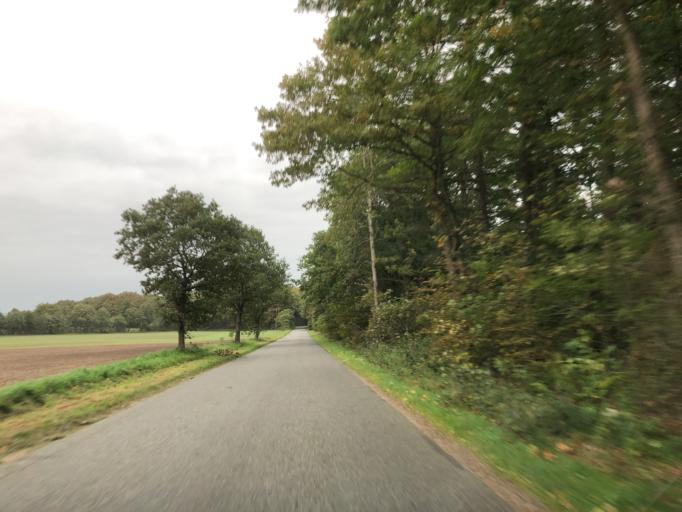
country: DK
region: Central Jutland
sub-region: Viborg Kommune
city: Viborg
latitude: 56.4200
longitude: 9.3212
